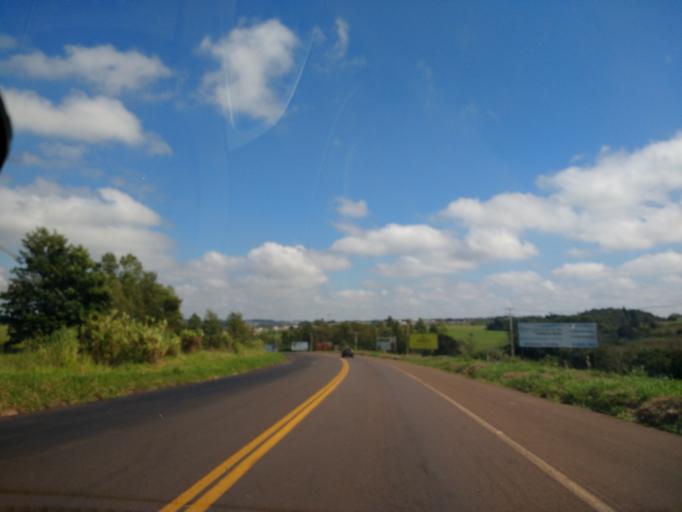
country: BR
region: Parana
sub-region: Umuarama
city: Umuarama
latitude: -23.7706
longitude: -53.2489
